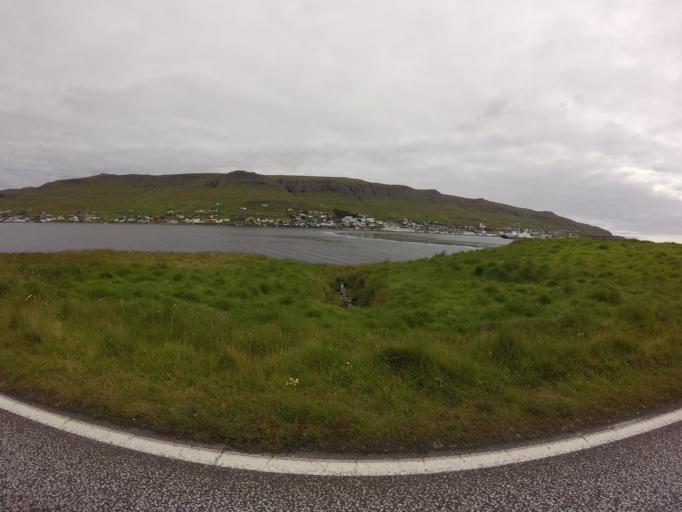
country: FO
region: Suduroy
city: Tvoroyri
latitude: 61.5504
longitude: -6.8270
